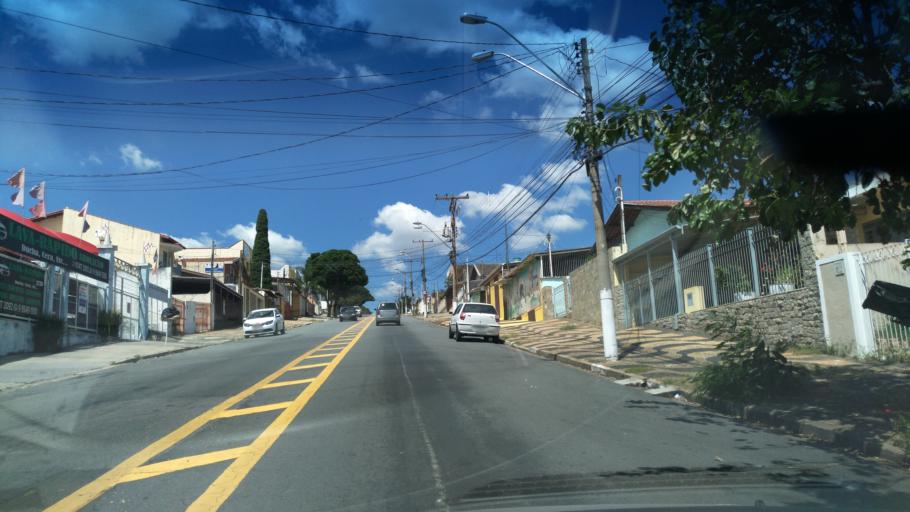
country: BR
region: Sao Paulo
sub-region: Campinas
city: Campinas
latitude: -22.9315
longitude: -47.0369
